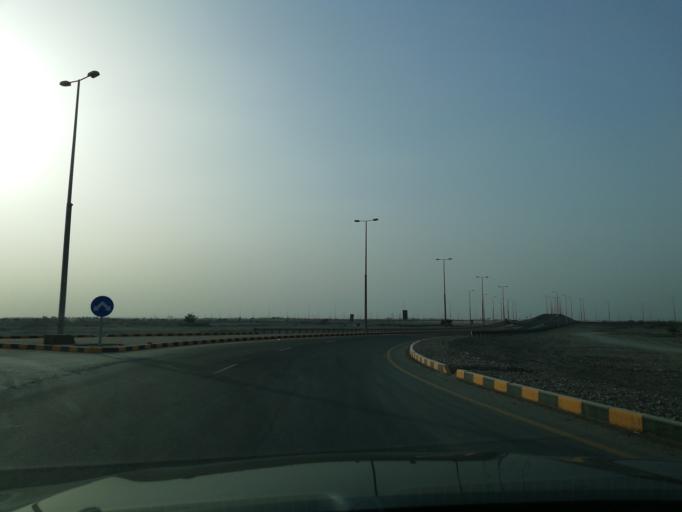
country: OM
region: Al Batinah
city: Barka'
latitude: 23.6141
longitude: 57.9099
